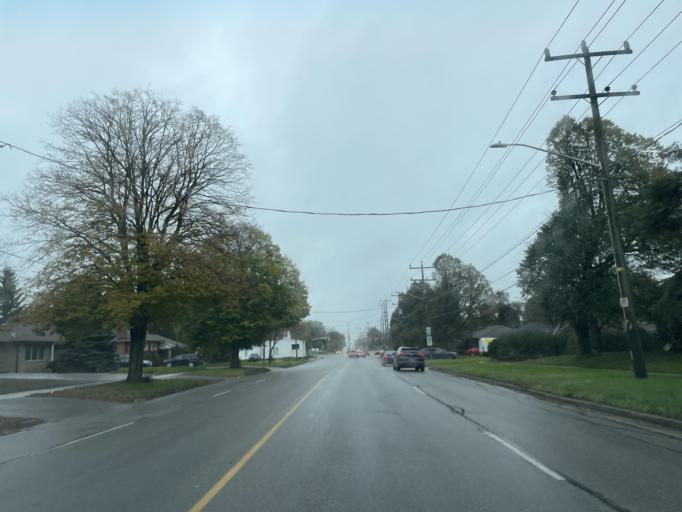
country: CA
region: Ontario
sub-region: Wellington County
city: Guelph
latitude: 43.5726
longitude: -80.2529
